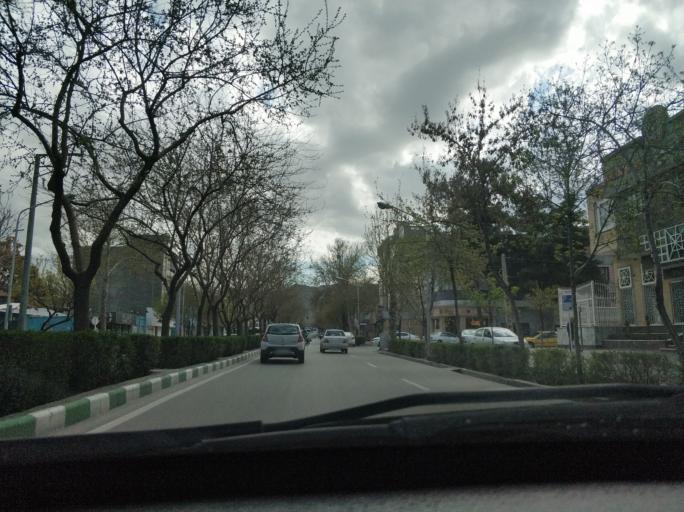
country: IR
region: Razavi Khorasan
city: Mashhad
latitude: 36.2726
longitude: 59.5905
